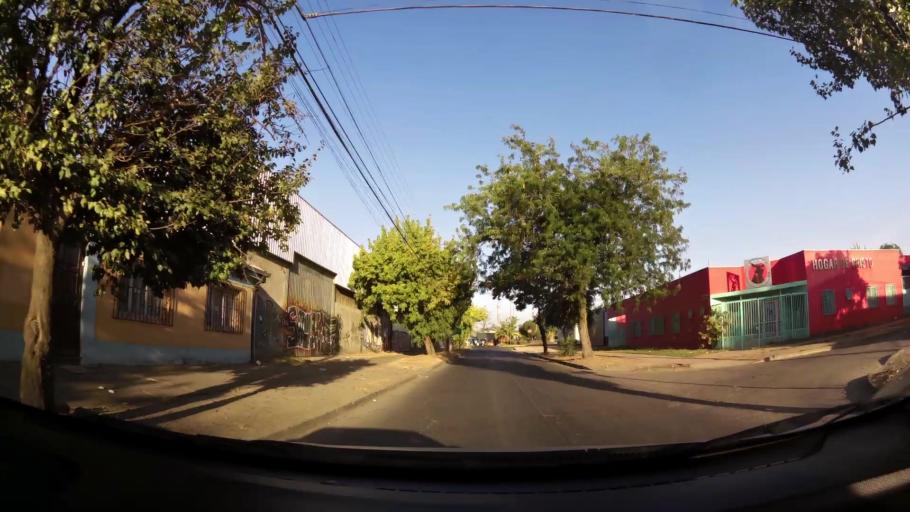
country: CL
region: Maule
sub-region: Provincia de Talca
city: Talca
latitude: -35.4312
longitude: -71.6410
